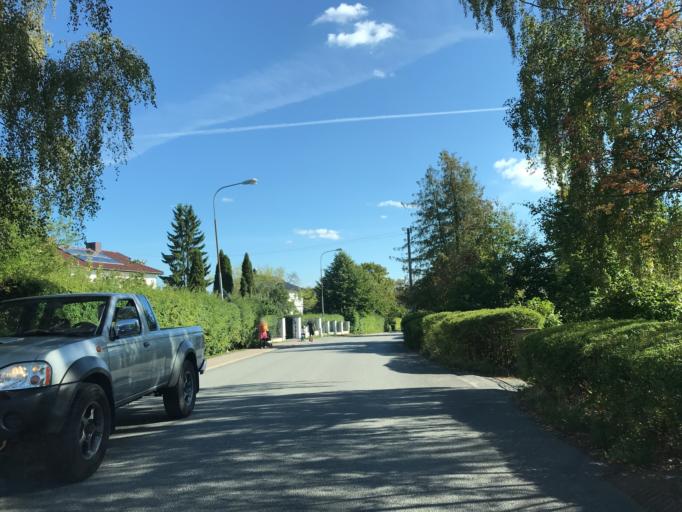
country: SE
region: Stockholm
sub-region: Sollentuna Kommun
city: Sollentuna
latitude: 59.4163
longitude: 17.9808
